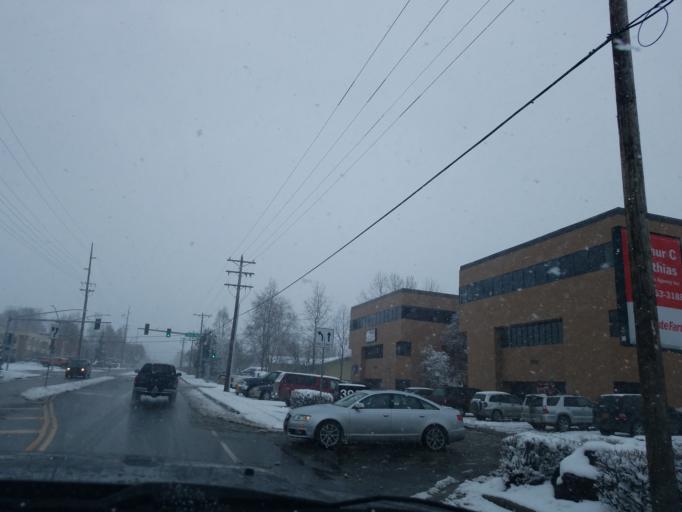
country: US
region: Alaska
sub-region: Anchorage Municipality
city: Anchorage
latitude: 61.1853
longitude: -149.8980
